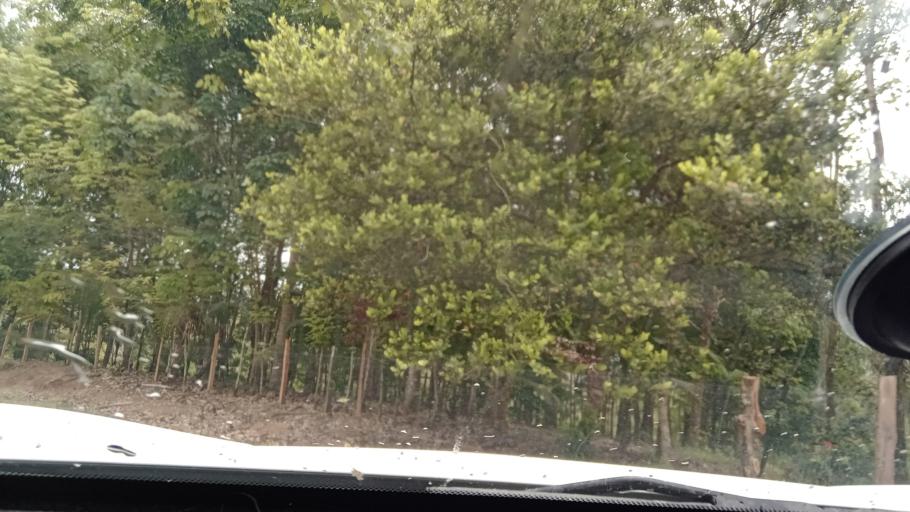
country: MX
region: Veracruz
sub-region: Uxpanapa
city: Poblado 10
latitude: 17.4504
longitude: -94.0889
